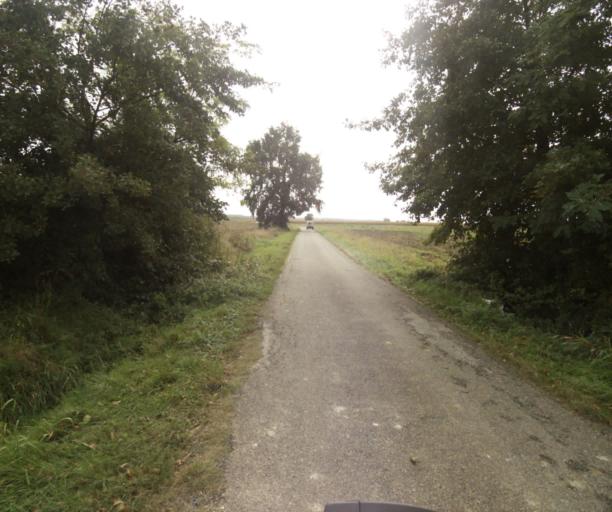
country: FR
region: Midi-Pyrenees
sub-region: Departement du Tarn-et-Garonne
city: Finhan
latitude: 43.9135
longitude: 1.2474
